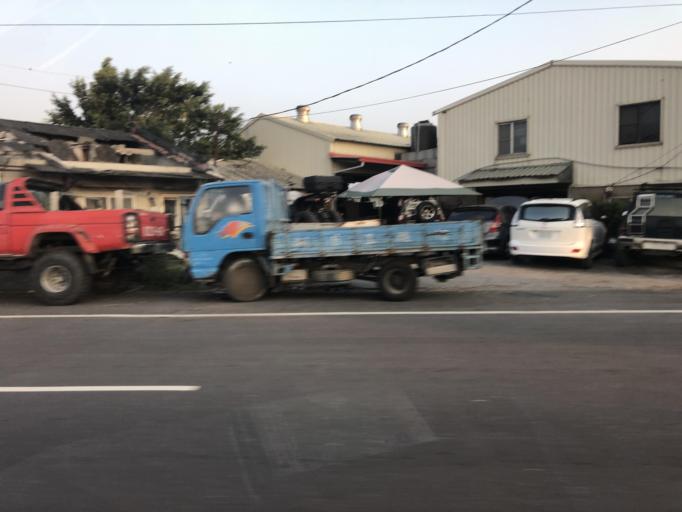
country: TW
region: Taiwan
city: Xinying
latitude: 23.1988
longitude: 120.2664
